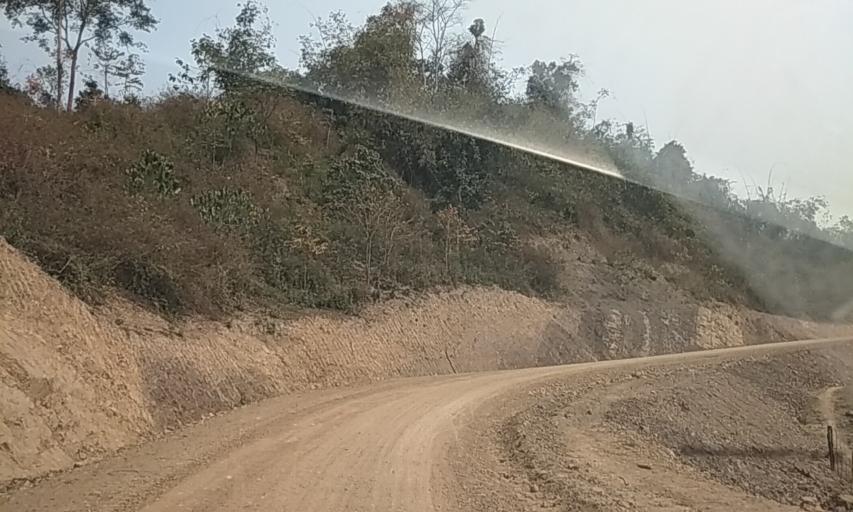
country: VN
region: Huyen Dien Bien
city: Dien Bien Phu
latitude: 21.4219
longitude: 102.7597
